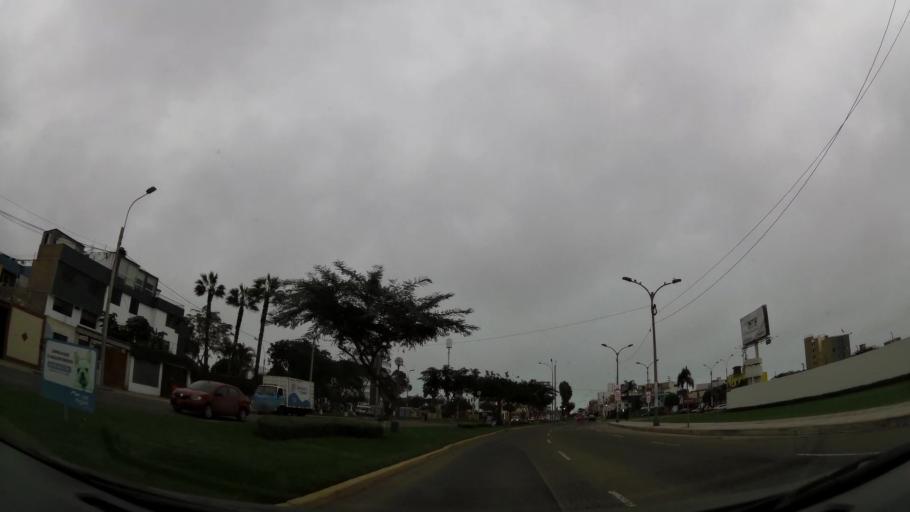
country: PE
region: Callao
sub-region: Callao
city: Callao
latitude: -12.0711
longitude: -77.1048
